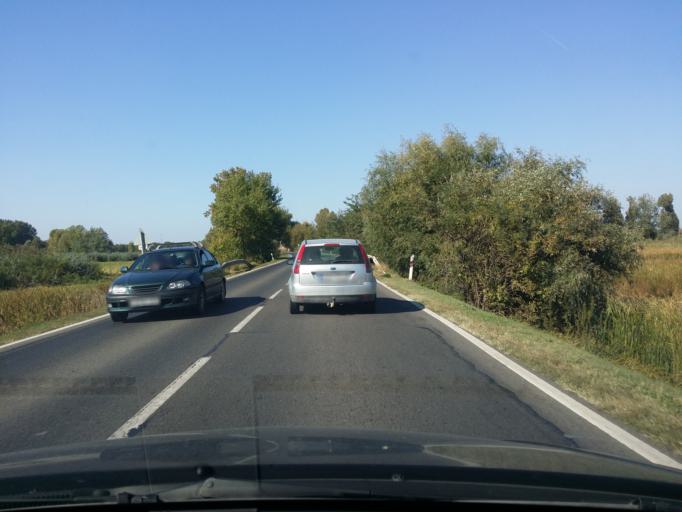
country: HU
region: Bacs-Kiskun
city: Lakitelek
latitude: 46.8705
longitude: 20.0373
